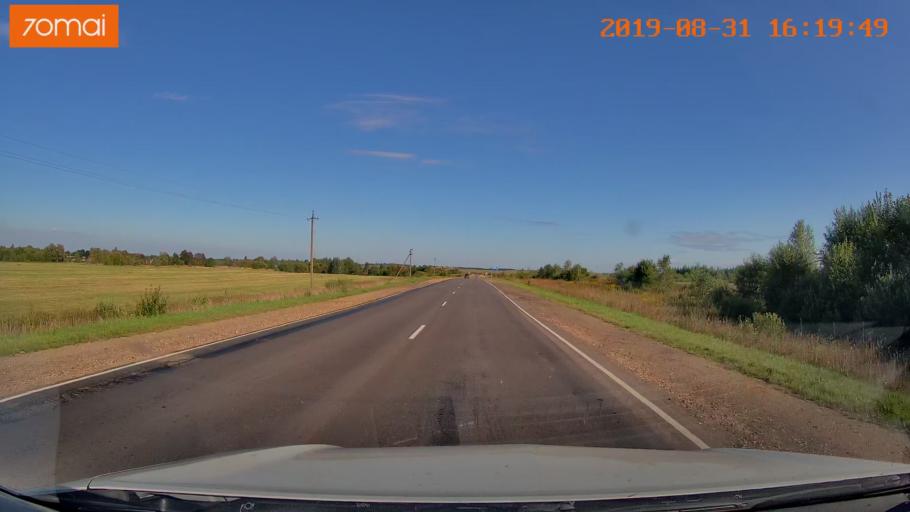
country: RU
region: Kaluga
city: Nikola-Lenivets
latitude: 54.5263
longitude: 35.5882
